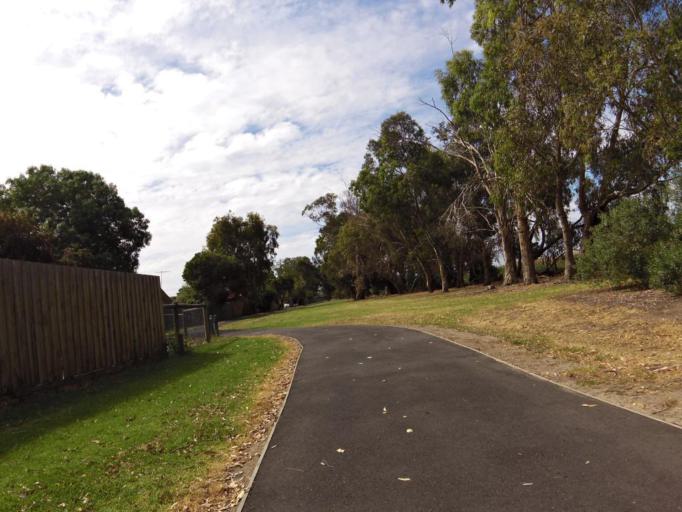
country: AU
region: Victoria
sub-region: Frankston
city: Seaford
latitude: -38.0970
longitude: 145.1350
